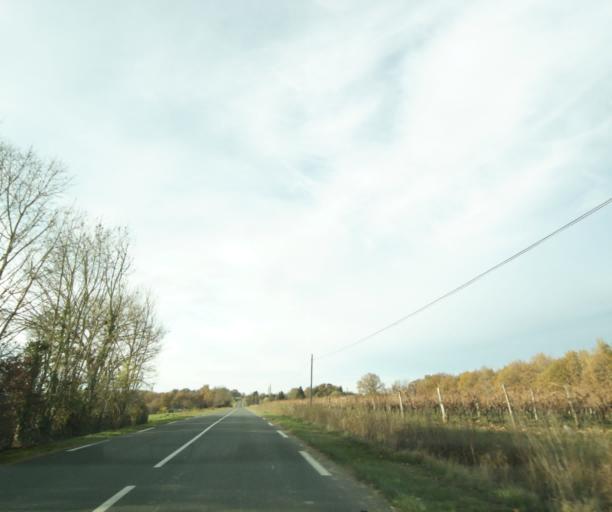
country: FR
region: Midi-Pyrenees
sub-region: Departement du Gers
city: Cazaubon
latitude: 43.8898
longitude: 0.0056
